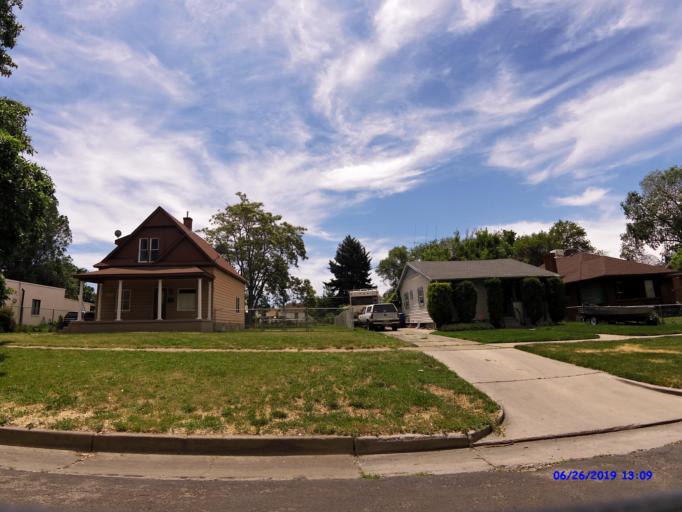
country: US
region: Utah
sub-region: Weber County
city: Ogden
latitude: 41.2121
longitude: -111.9613
